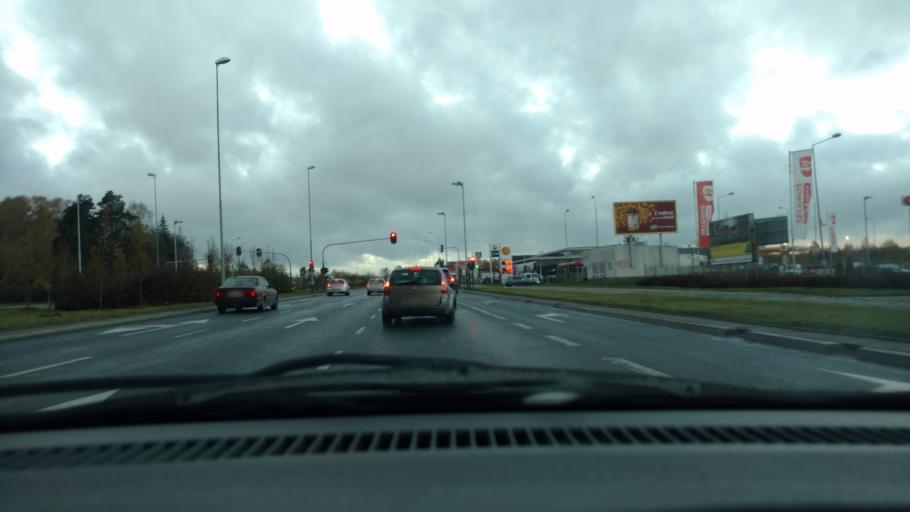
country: PL
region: Lodz Voivodeship
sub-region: Powiat lodzki wschodni
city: Andrespol
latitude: 51.7524
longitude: 19.5837
